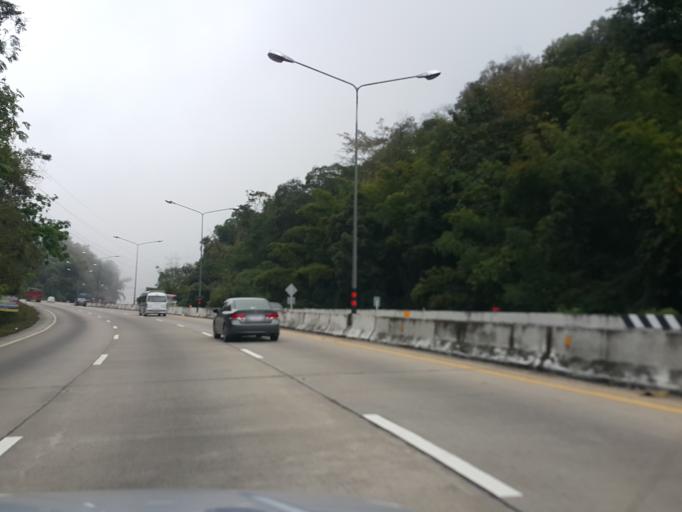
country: TH
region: Lamphun
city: Mae Tha
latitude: 18.4297
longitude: 99.2074
